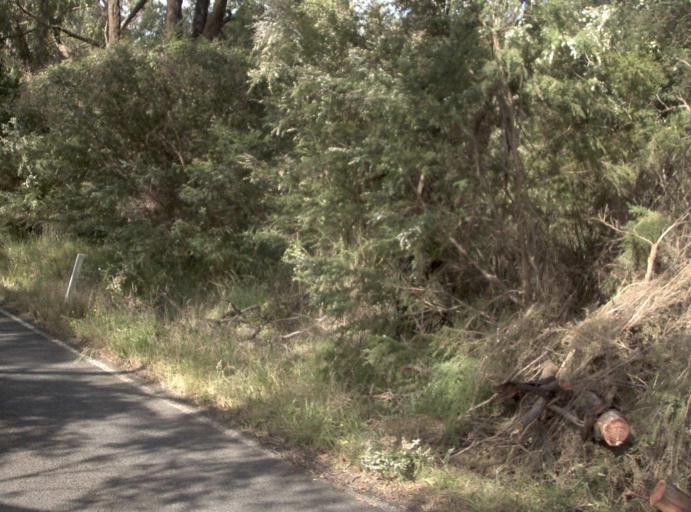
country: AU
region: Victoria
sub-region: Latrobe
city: Morwell
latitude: -38.1925
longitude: 146.4035
